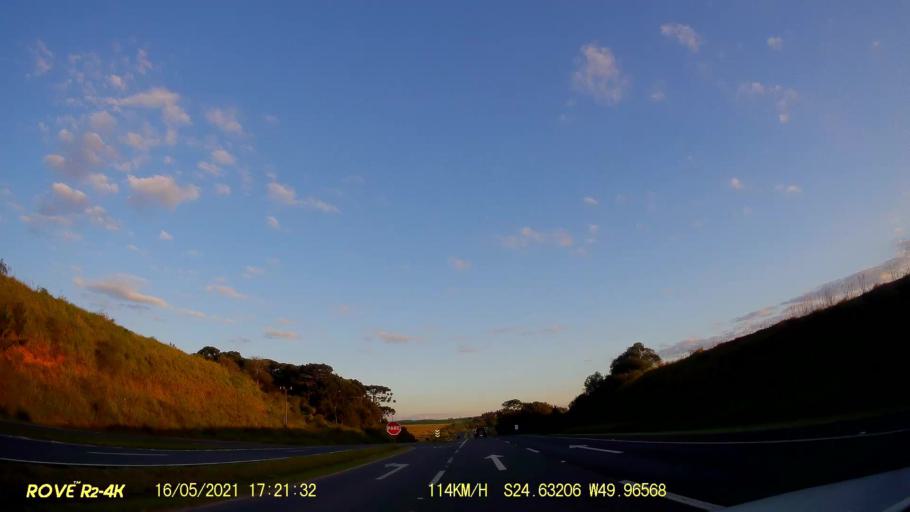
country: BR
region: Parana
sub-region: Pirai Do Sul
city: Pirai do Sul
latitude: -24.6325
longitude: -49.9657
